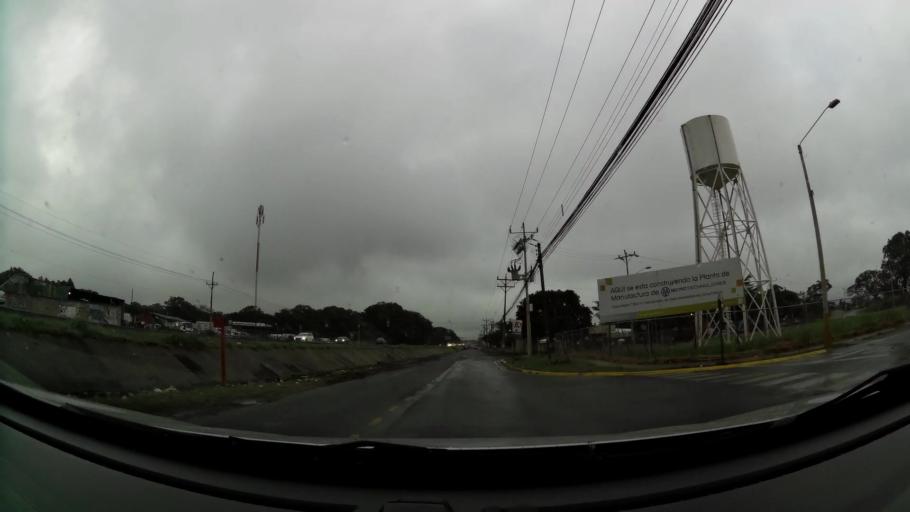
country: CR
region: Alajuela
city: Carrillos
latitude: 9.9957
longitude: -84.2634
